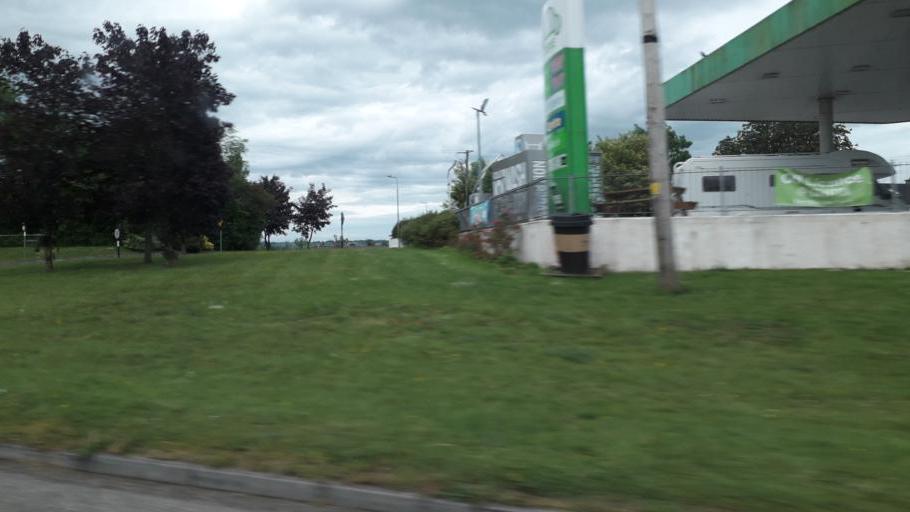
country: IE
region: Leinster
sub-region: County Carlow
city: Bagenalstown
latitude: 52.7387
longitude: -6.9859
